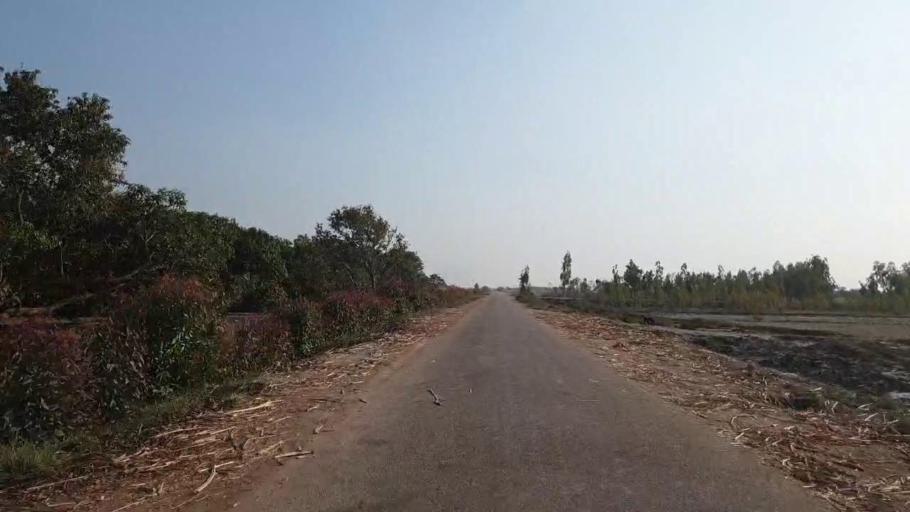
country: PK
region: Sindh
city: Tando Allahyar
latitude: 25.5942
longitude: 68.6190
